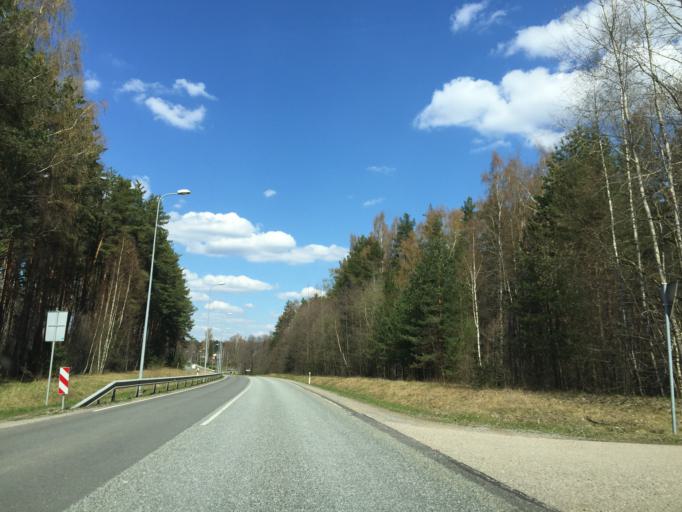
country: LV
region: Saulkrastu
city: Saulkrasti
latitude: 57.2268
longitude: 24.3926
